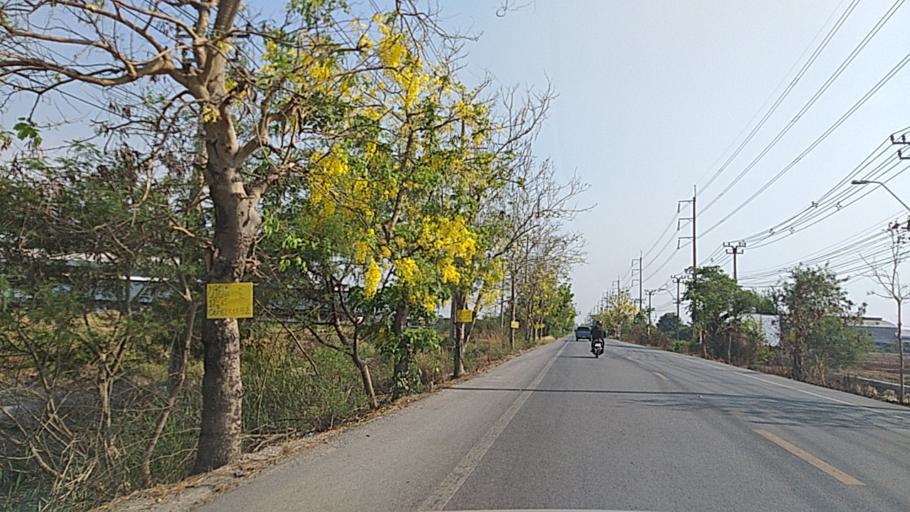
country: TH
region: Nonthaburi
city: Sai Noi
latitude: 14.0412
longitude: 100.3121
